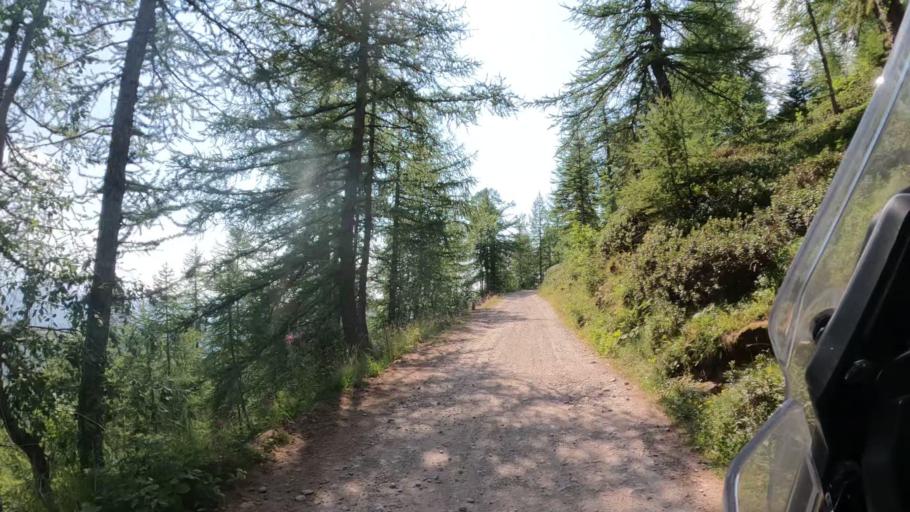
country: IT
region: Piedmont
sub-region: Provincia di Cuneo
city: Briga Alta
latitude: 44.1069
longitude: 7.7079
